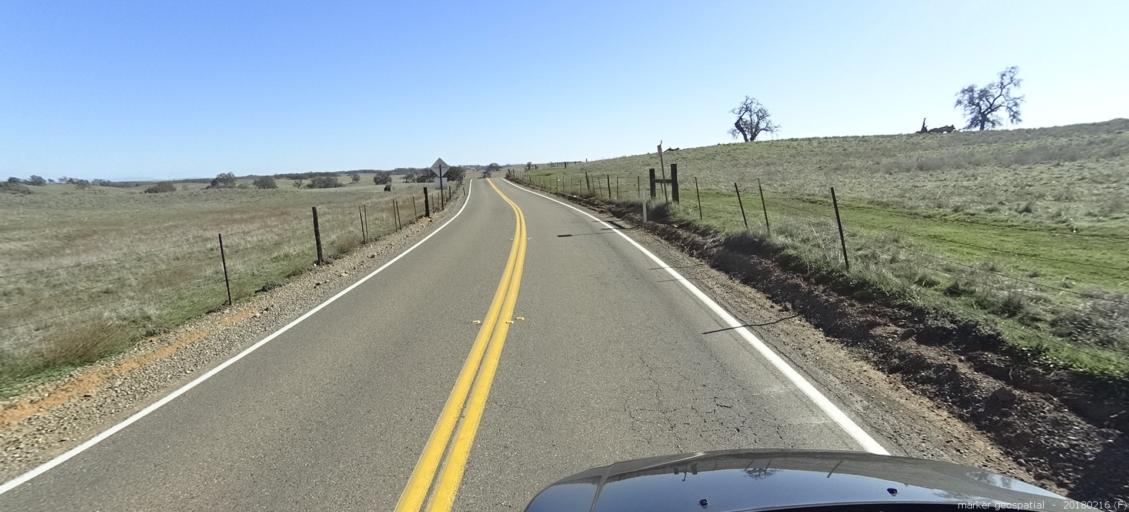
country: US
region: California
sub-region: Sacramento County
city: Rancho Murieta
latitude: 38.5677
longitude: -121.1303
